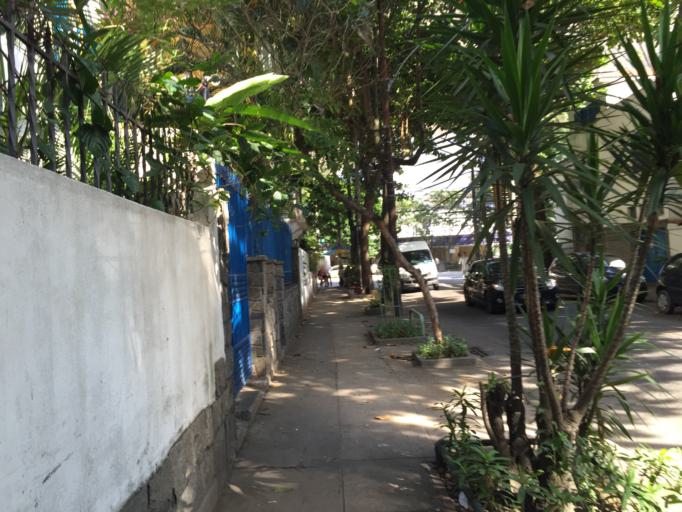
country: BR
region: Rio de Janeiro
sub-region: Rio De Janeiro
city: Rio de Janeiro
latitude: -22.9540
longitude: -43.1674
